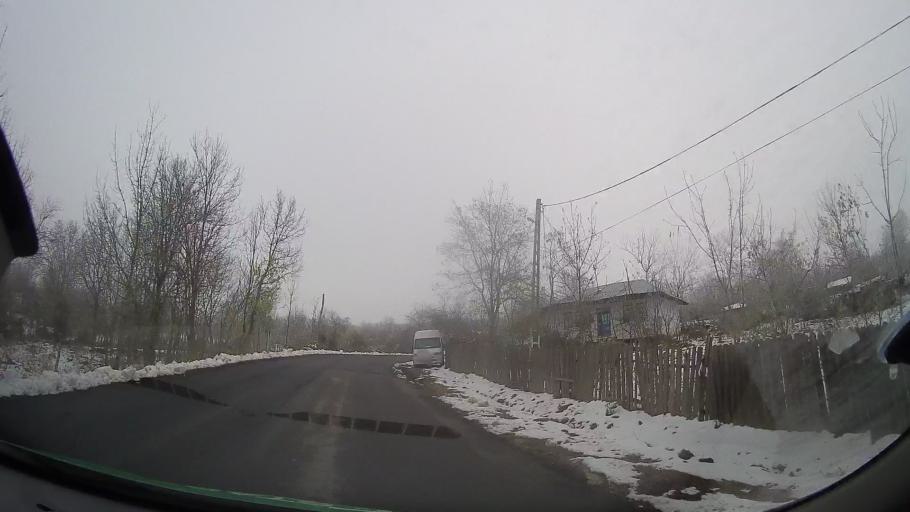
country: RO
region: Vaslui
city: Coroiesti
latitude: 46.2096
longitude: 27.4412
